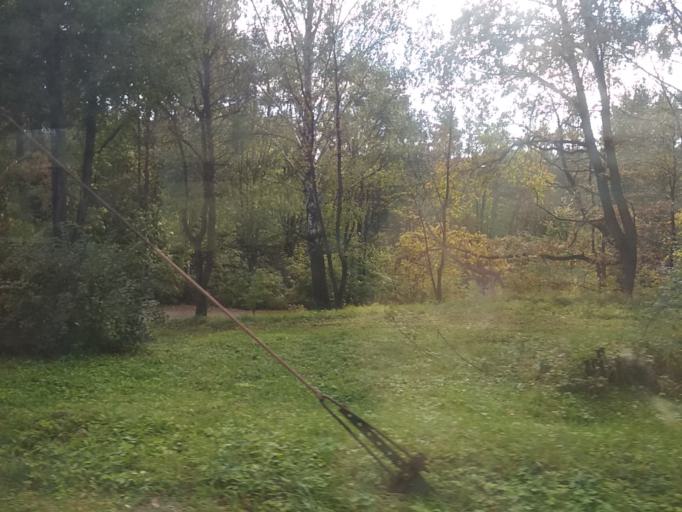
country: BY
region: Minsk
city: Machulishchy
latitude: 53.7851
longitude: 27.6035
